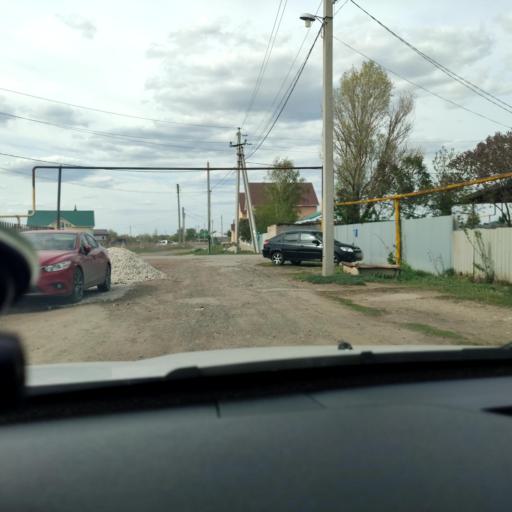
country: RU
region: Samara
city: Spiridonovka
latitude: 53.1601
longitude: 50.6470
